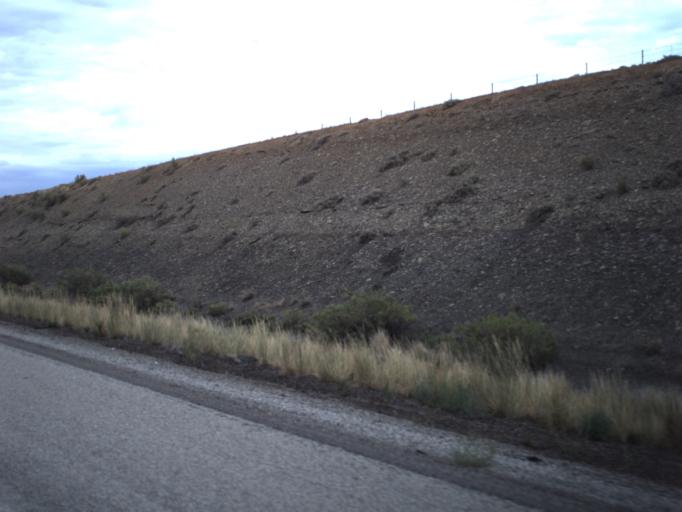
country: US
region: Colorado
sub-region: Mesa County
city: Loma
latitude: 39.0266
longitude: -109.2931
